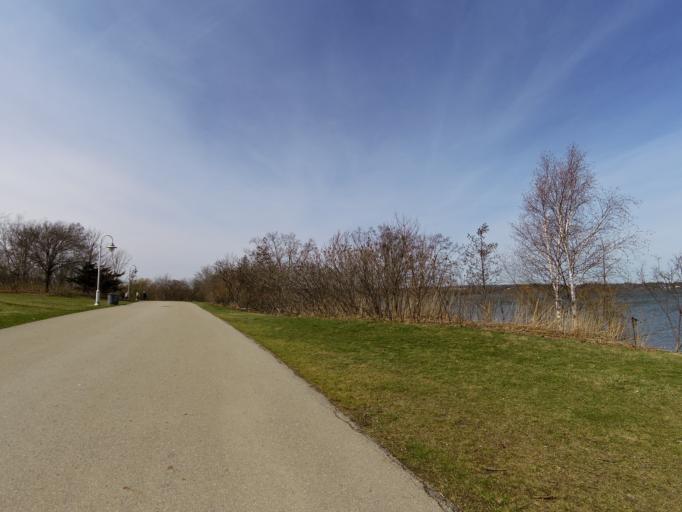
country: CA
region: Ontario
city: Hamilton
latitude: 43.2723
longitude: -79.8709
